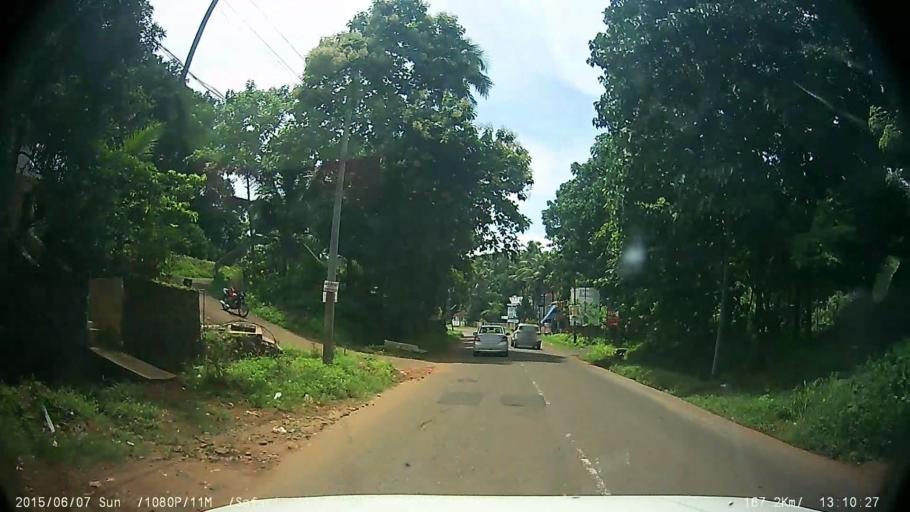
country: IN
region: Kerala
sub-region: Ernakulam
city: Muvattupuzha
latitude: 9.9413
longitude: 76.5759
